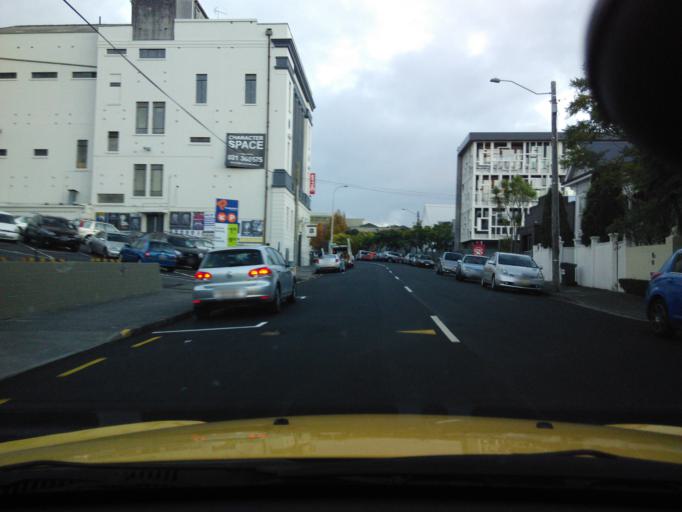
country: NZ
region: Auckland
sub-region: Auckland
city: Auckland
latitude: -36.8617
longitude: 174.7606
